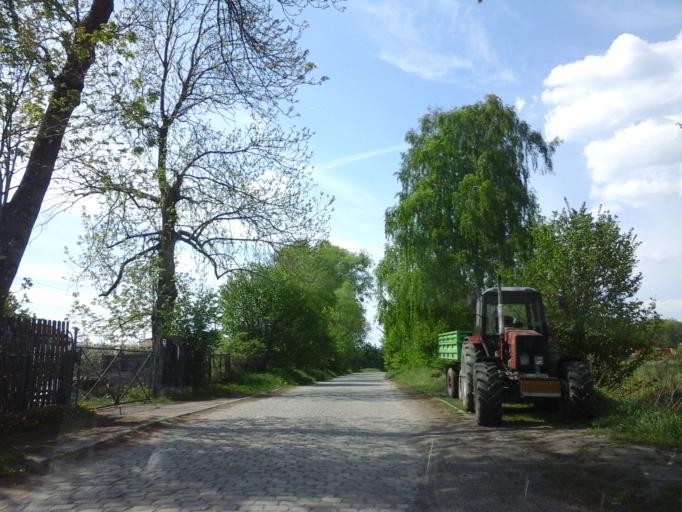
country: PL
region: West Pomeranian Voivodeship
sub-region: Powiat choszczenski
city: Choszczno
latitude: 53.1780
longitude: 15.4248
